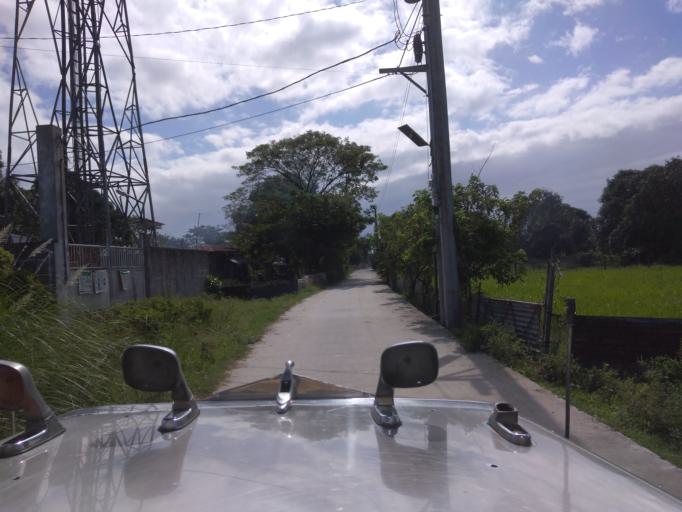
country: PH
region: Central Luzon
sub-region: Province of Pampanga
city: San Patricio
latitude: 15.0894
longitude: 120.7160
